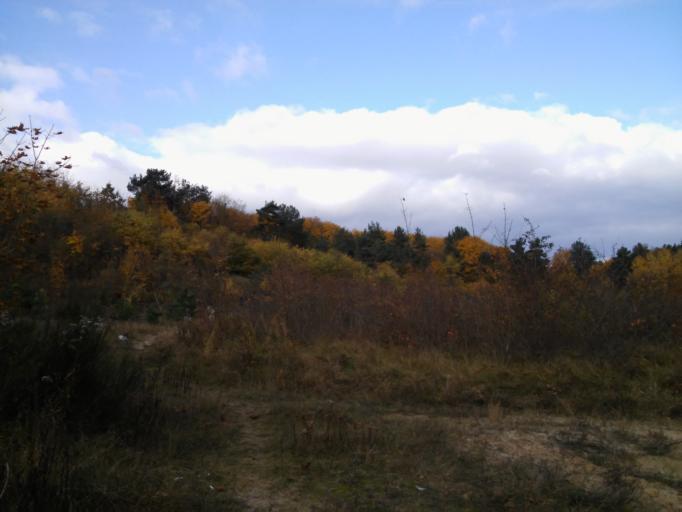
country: PL
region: Pomeranian Voivodeship
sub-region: Powiat gdanski
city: Kowale
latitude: 54.3670
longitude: 18.5782
